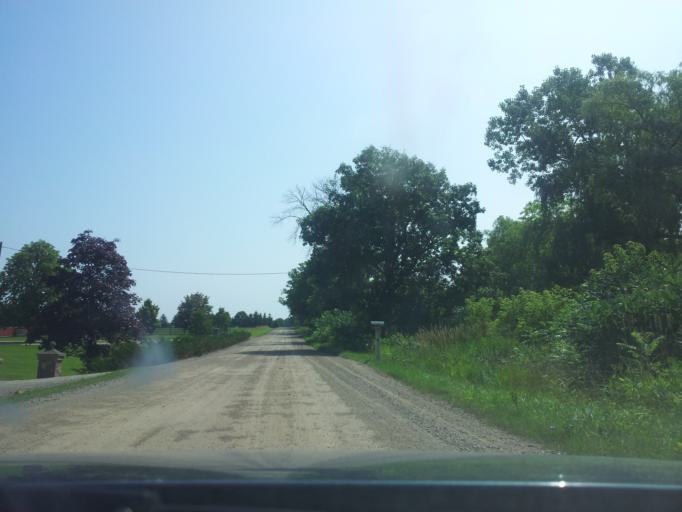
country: CA
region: Ontario
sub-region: Oxford County
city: Woodstock
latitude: 42.9569
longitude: -80.6014
